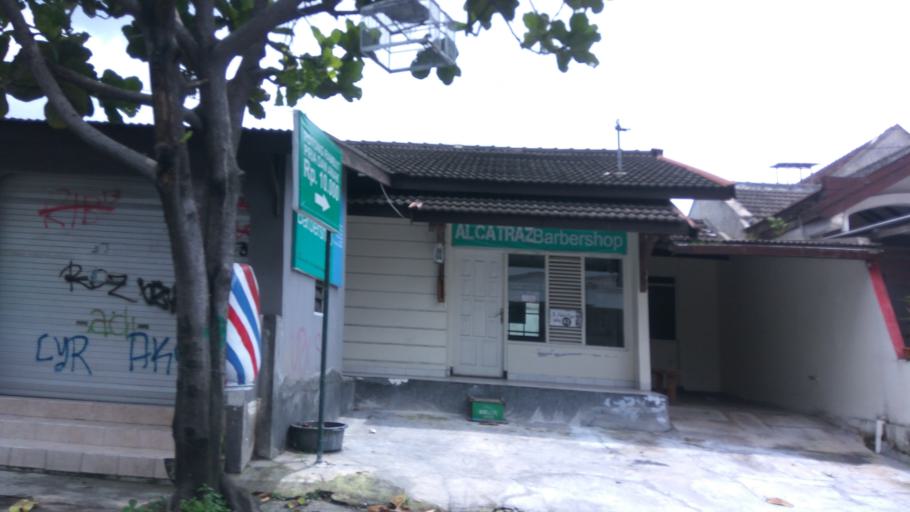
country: ID
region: Daerah Istimewa Yogyakarta
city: Depok
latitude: -7.7415
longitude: 110.4081
